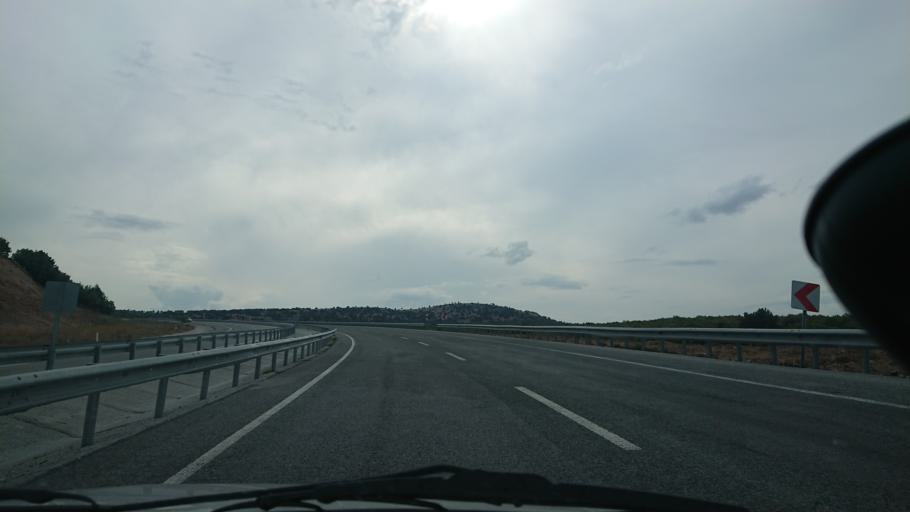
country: TR
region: Kuetahya
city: Aslanapa
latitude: 39.2761
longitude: 29.9319
